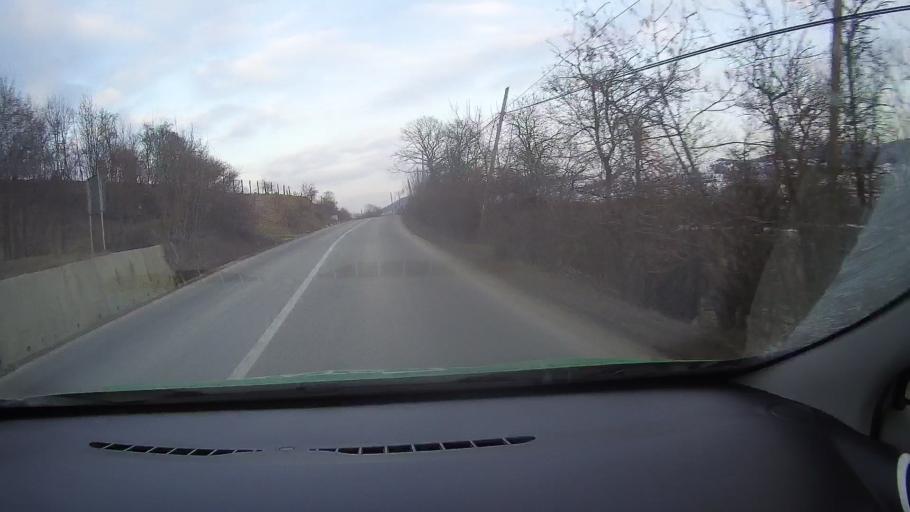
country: RO
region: Harghita
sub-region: Comuna Simonesti
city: Simonesti
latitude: 46.3569
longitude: 25.1549
